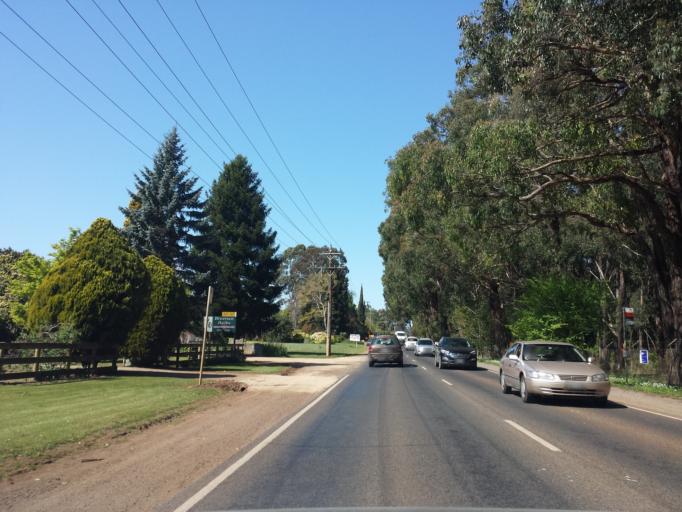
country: AU
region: Victoria
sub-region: Yarra Ranges
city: Monbulk
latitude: -37.8483
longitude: 145.4230
